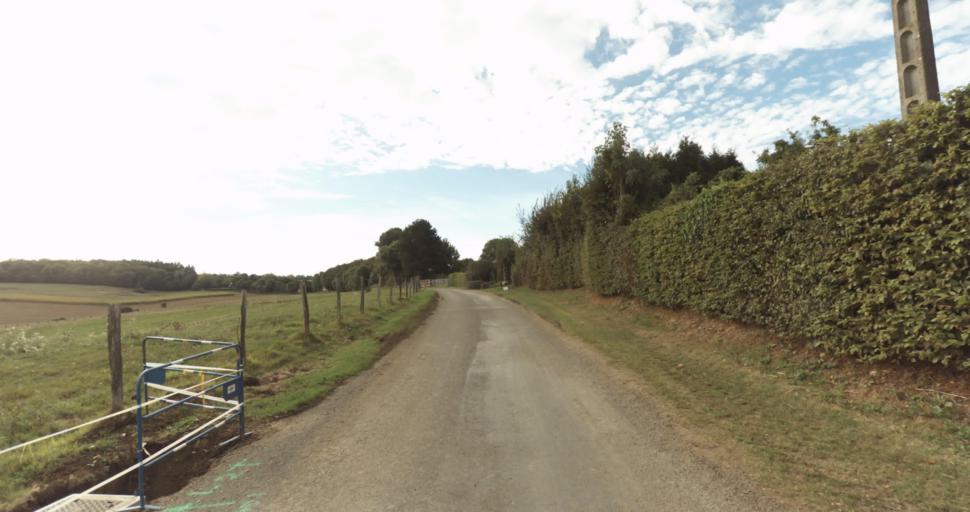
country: FR
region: Lower Normandy
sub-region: Departement de l'Orne
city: Vimoutiers
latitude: 48.8517
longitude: 0.2323
